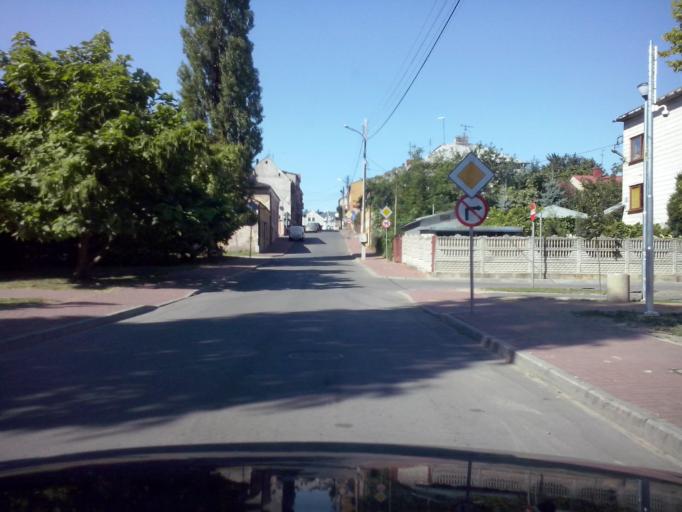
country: PL
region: Swietokrzyskie
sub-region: Powiat kielecki
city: Chmielnik
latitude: 50.6127
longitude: 20.7521
